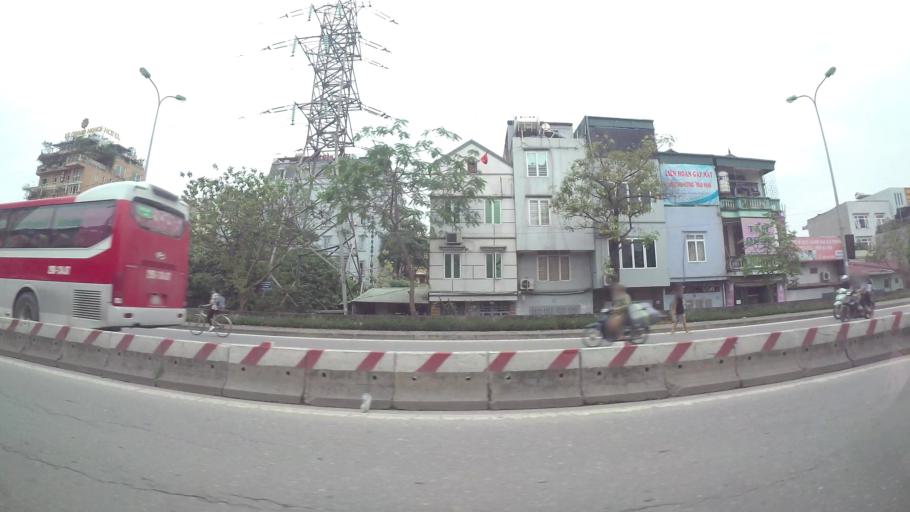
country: VN
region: Ha Noi
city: Hai BaTrung
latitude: 21.0096
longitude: 105.8651
